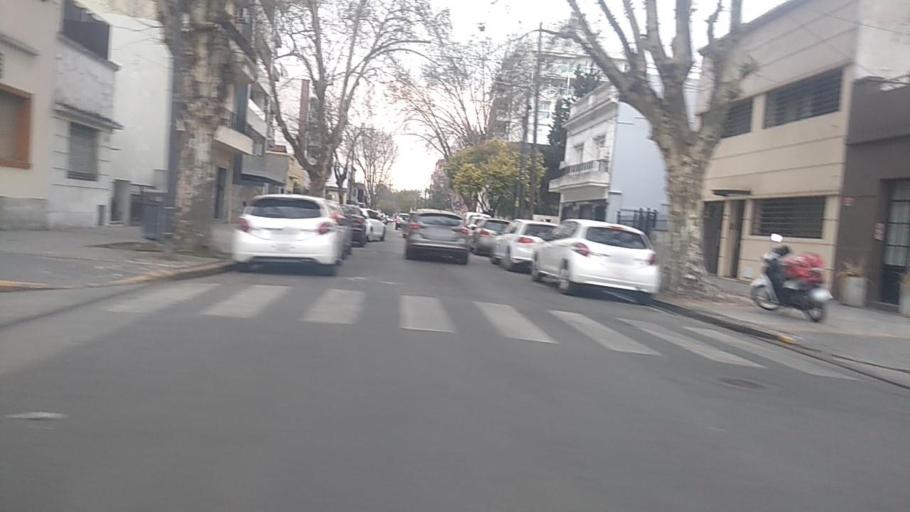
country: AR
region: Buenos Aires F.D.
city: Villa Santa Rita
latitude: -34.5993
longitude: -58.4988
